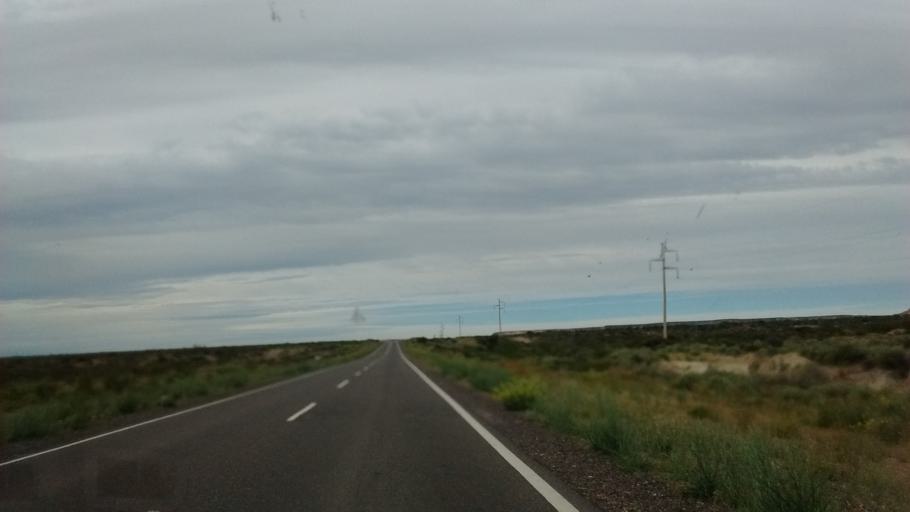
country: AR
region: Rio Negro
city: Catriel
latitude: -38.1487
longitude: -67.9426
